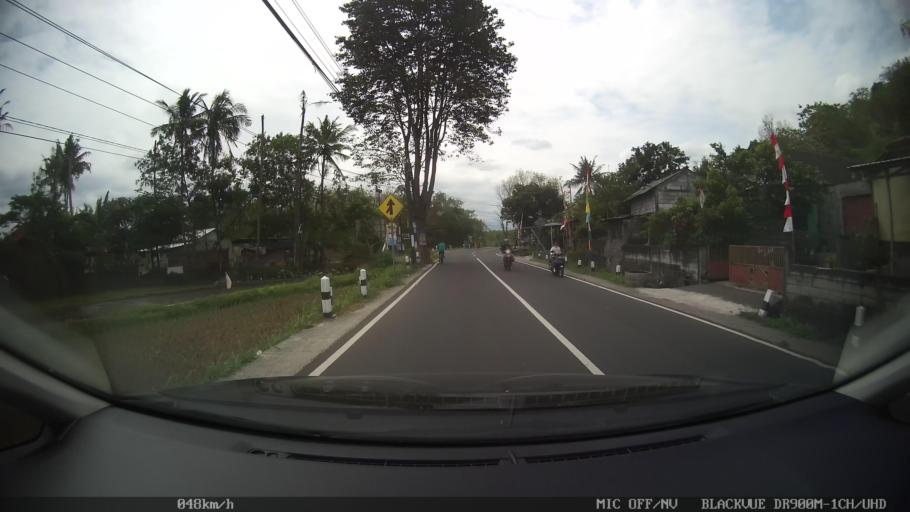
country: ID
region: Central Java
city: Candi Prambanan
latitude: -7.7734
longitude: 110.4813
